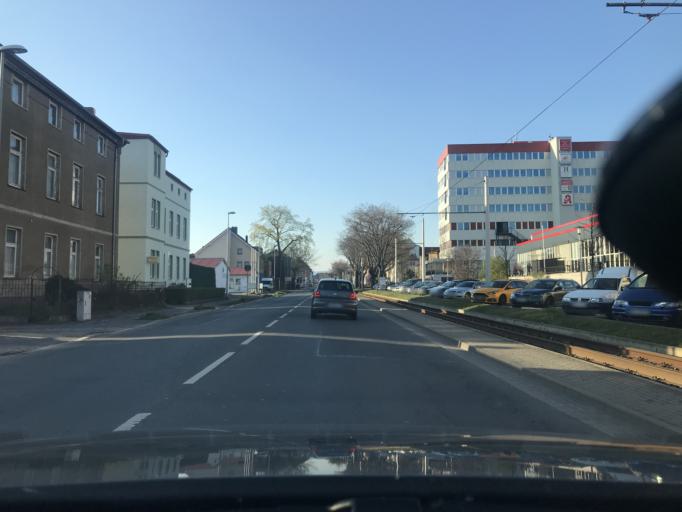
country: DE
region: Thuringia
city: Nordhausen
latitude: 51.4998
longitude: 10.7881
